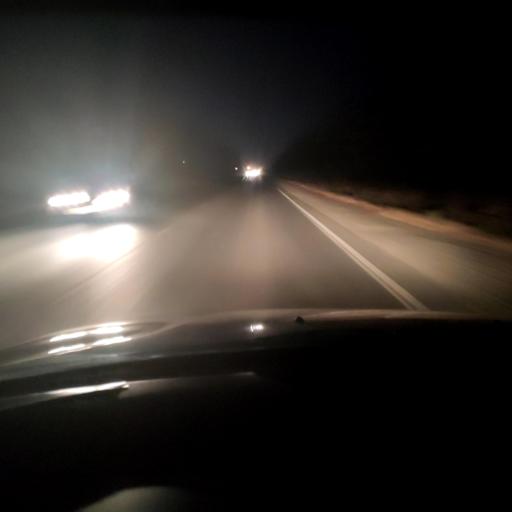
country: RU
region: Samara
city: Tol'yatti
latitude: 53.5588
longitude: 49.3606
